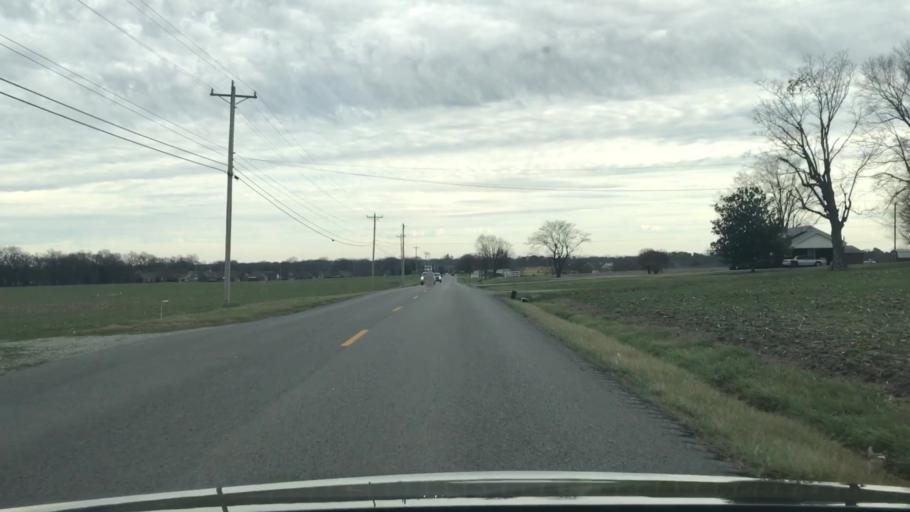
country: US
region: Kentucky
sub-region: Christian County
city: Hopkinsville
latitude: 36.8612
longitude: -87.5333
